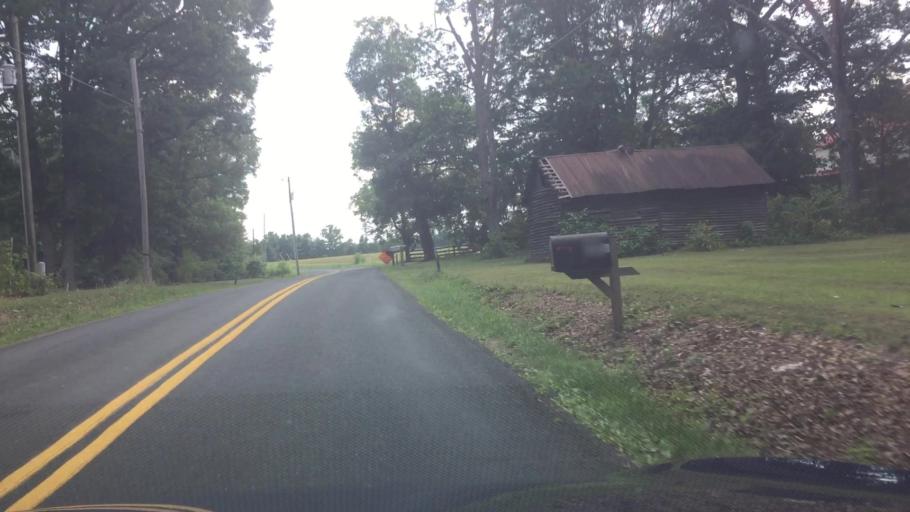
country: US
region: Virginia
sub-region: Appomattox County
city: Appomattox
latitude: 37.2865
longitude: -78.8518
